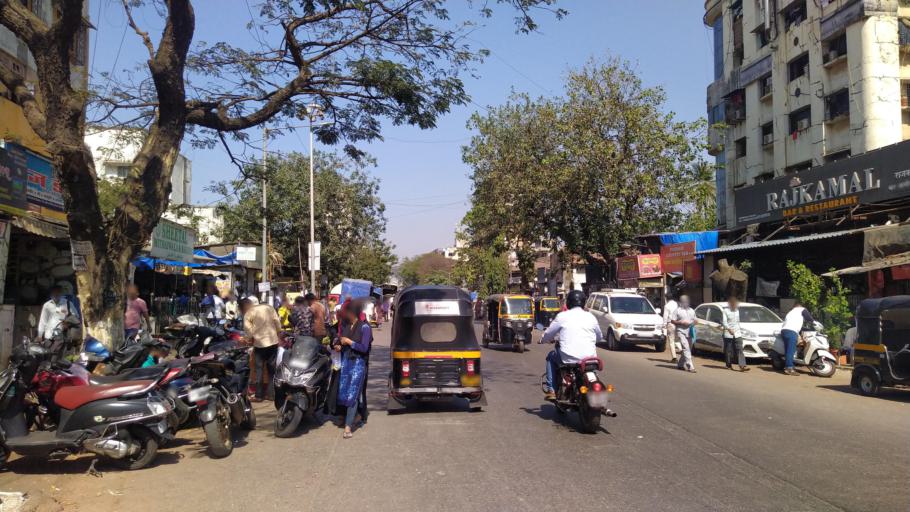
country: IN
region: Maharashtra
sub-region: Mumbai Suburban
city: Mumbai
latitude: 19.0697
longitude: 72.8791
